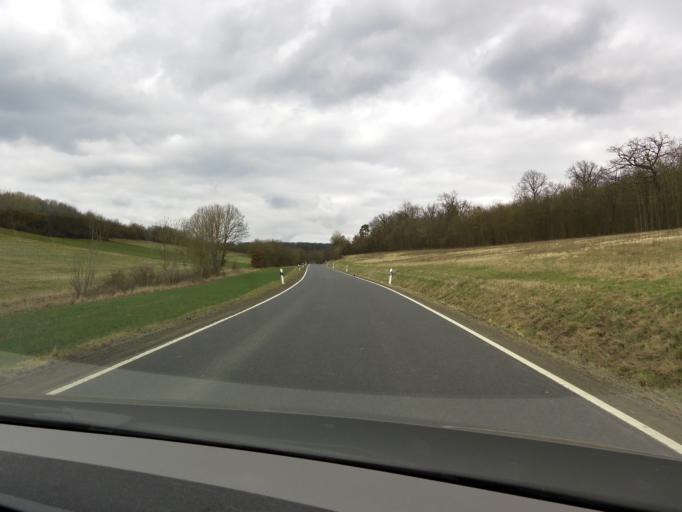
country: DE
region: Bavaria
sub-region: Regierungsbezirk Unterfranken
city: Rimpar
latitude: 49.8668
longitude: 9.9672
